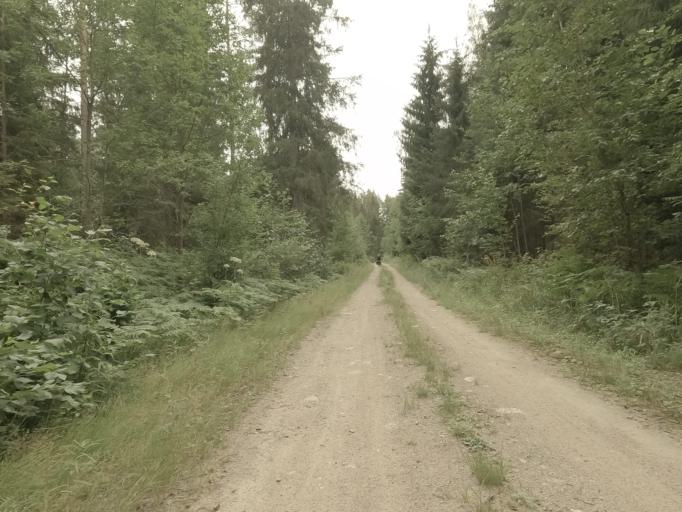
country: RU
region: Leningrad
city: Kamennogorsk
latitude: 61.0693
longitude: 29.1662
